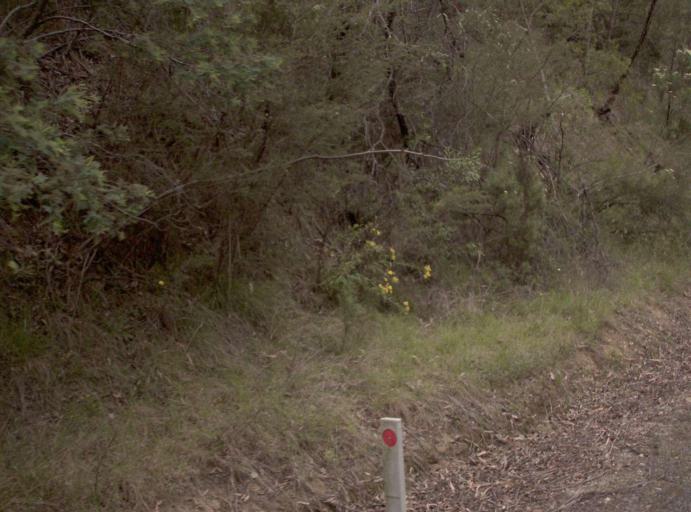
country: AU
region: New South Wales
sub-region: Bombala
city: Bombala
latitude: -37.3619
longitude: 149.2025
